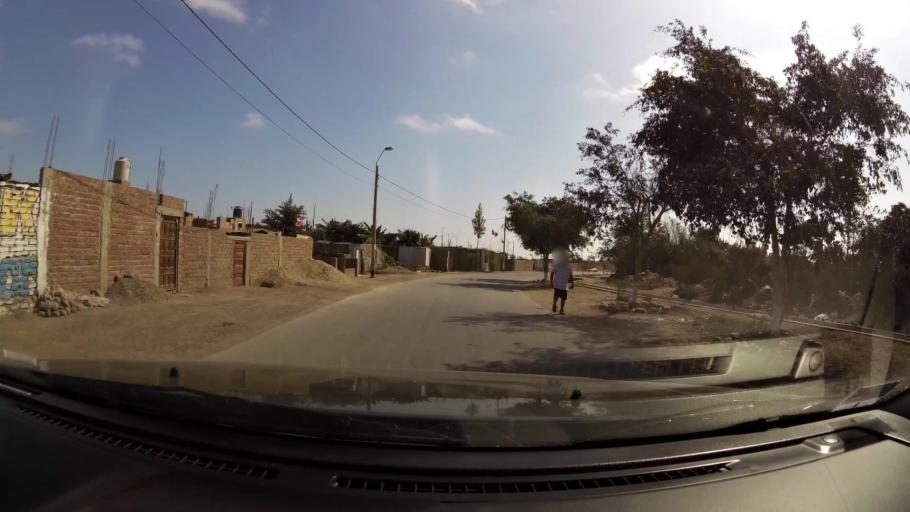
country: PE
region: Ica
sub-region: Provincia de Chincha
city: Sunampe
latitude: -13.4255
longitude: -76.1664
